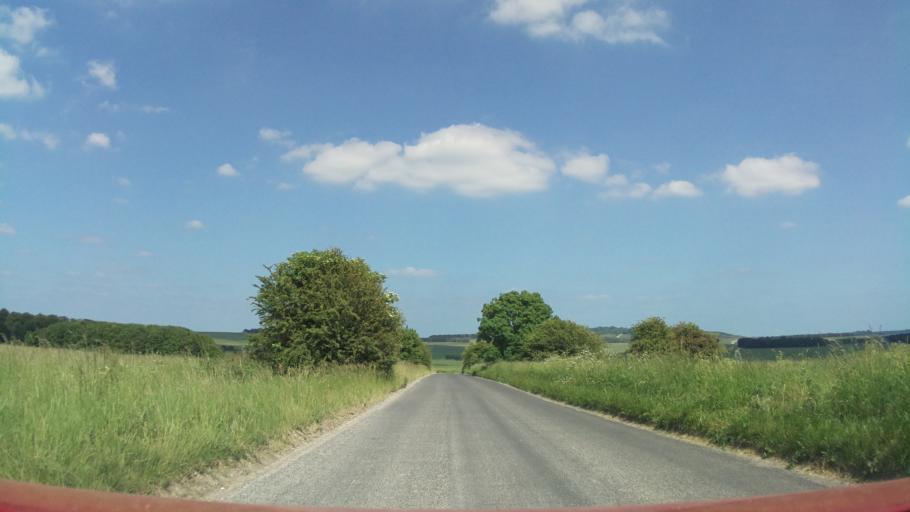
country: GB
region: England
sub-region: Wiltshire
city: Milston
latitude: 51.2540
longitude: -1.7404
